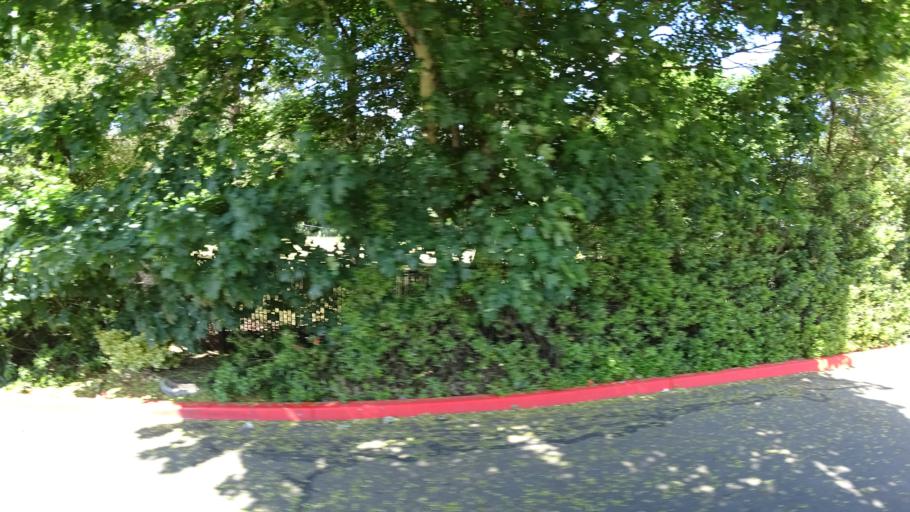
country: US
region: Oregon
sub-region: Clackamas County
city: Lake Oswego
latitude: 45.4339
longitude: -122.7016
